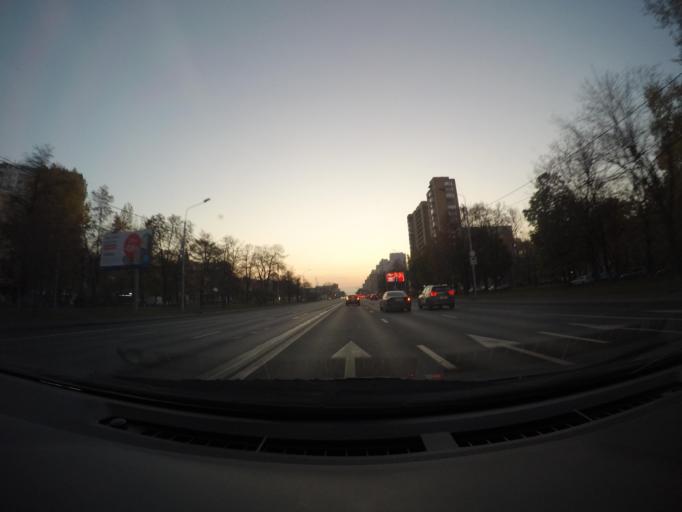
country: RU
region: Moscow
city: Novyye Kuz'minki
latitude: 55.7061
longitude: 37.7602
